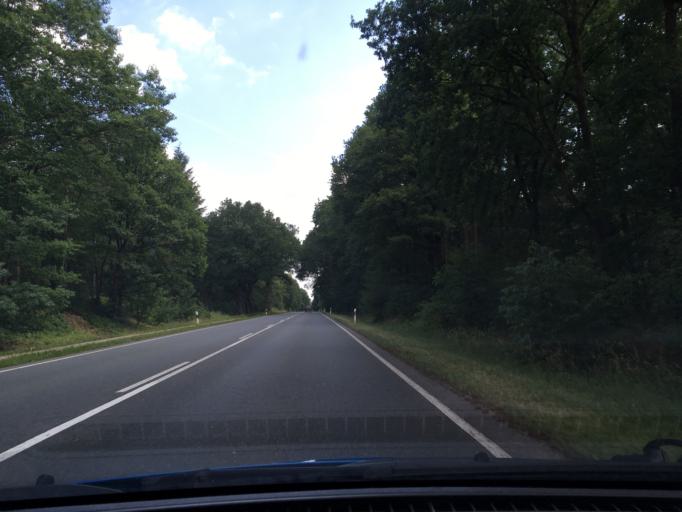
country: DE
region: Lower Saxony
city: Welle
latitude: 53.2763
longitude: 9.7982
